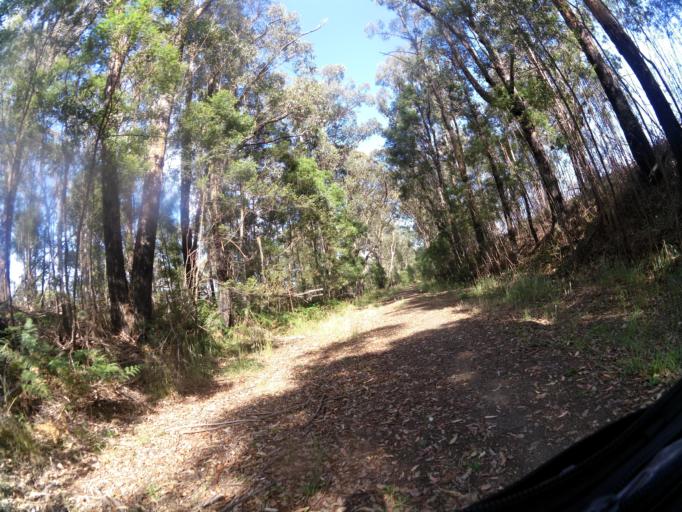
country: AU
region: Victoria
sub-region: East Gippsland
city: Lakes Entrance
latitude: -37.7514
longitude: 148.1894
